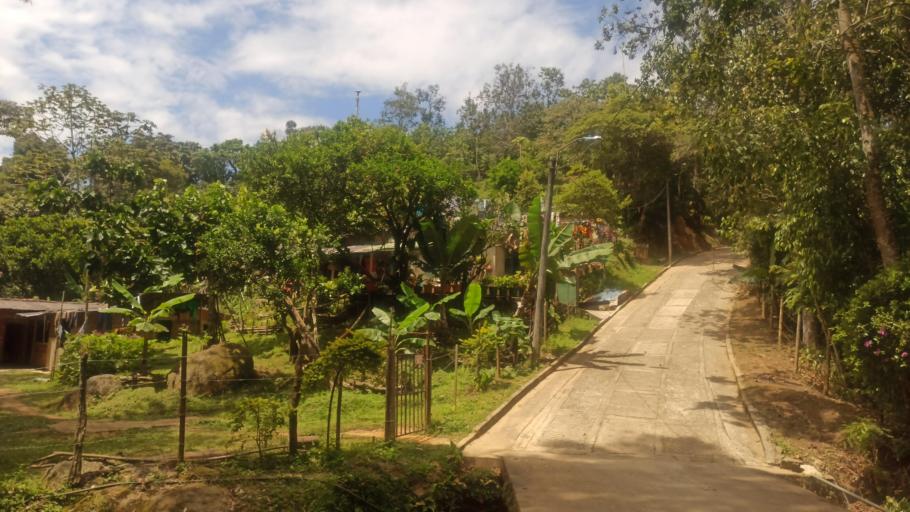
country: CO
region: Valle del Cauca
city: Jamundi
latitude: 3.1868
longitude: -76.6329
